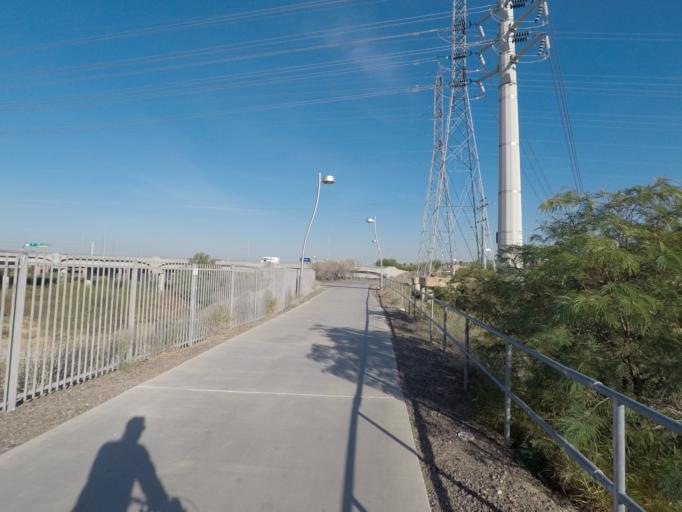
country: US
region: Arizona
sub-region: Maricopa County
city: Tempe
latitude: 33.4330
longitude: -111.9105
